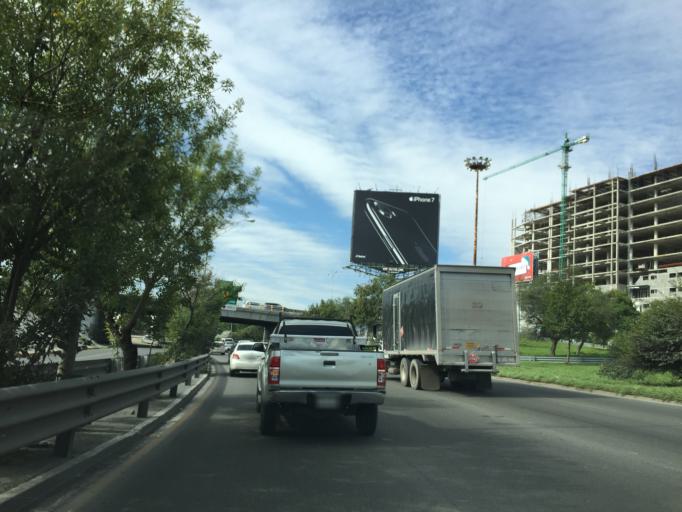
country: MX
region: Nuevo Leon
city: Guadalupe
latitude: 25.6909
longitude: -100.2438
